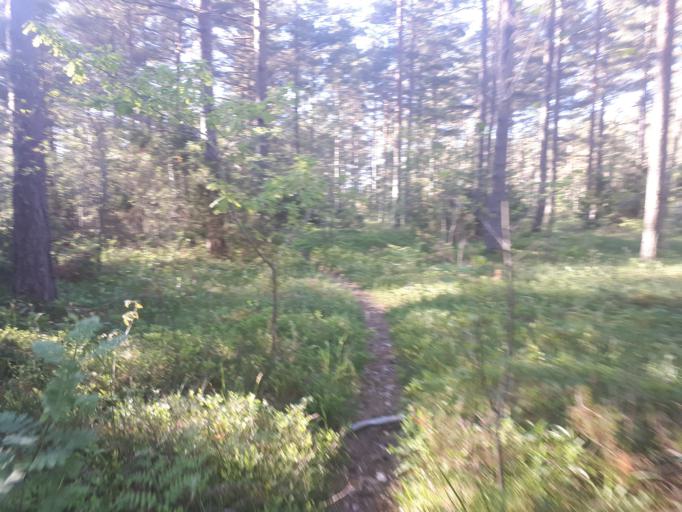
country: SE
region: Gotland
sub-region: Gotland
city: Visby
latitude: 57.6036
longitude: 18.2901
